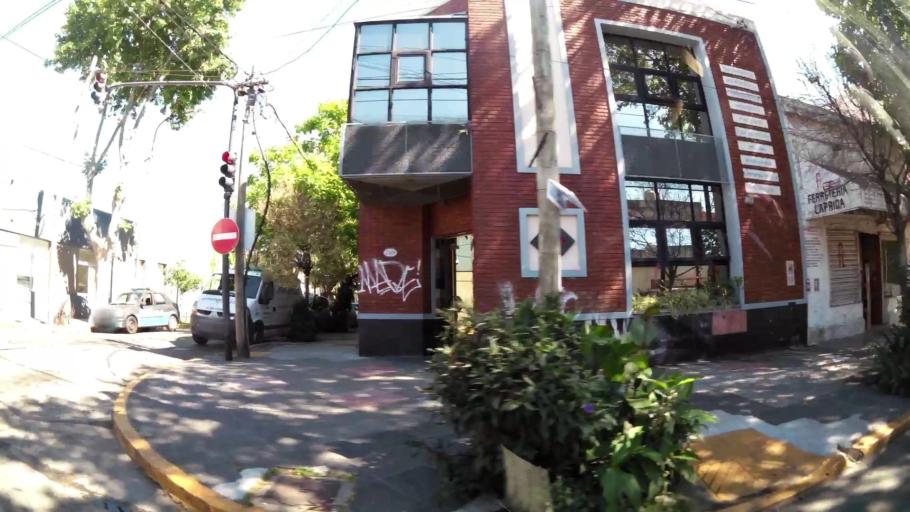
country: AR
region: Buenos Aires
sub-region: Partido de Vicente Lopez
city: Olivos
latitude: -34.5405
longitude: -58.4884
